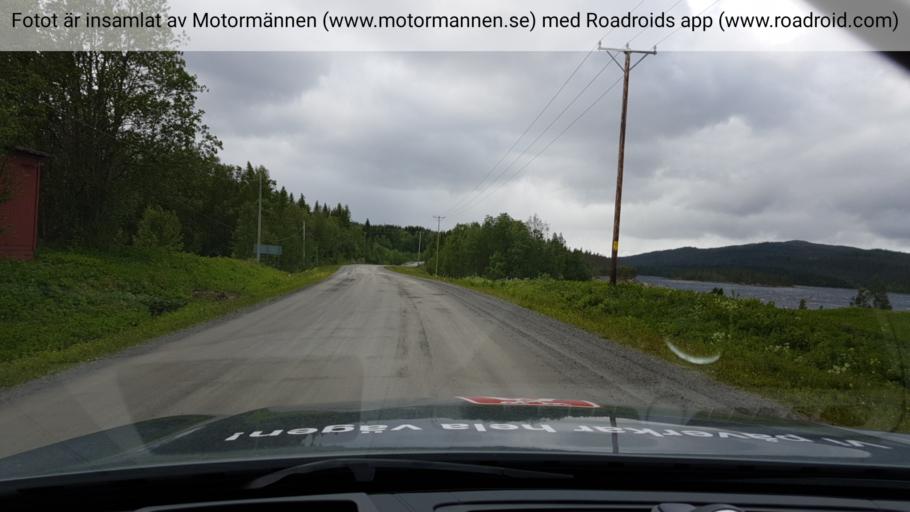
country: SE
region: Jaemtland
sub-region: Are Kommun
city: Are
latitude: 63.7081
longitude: 12.6449
